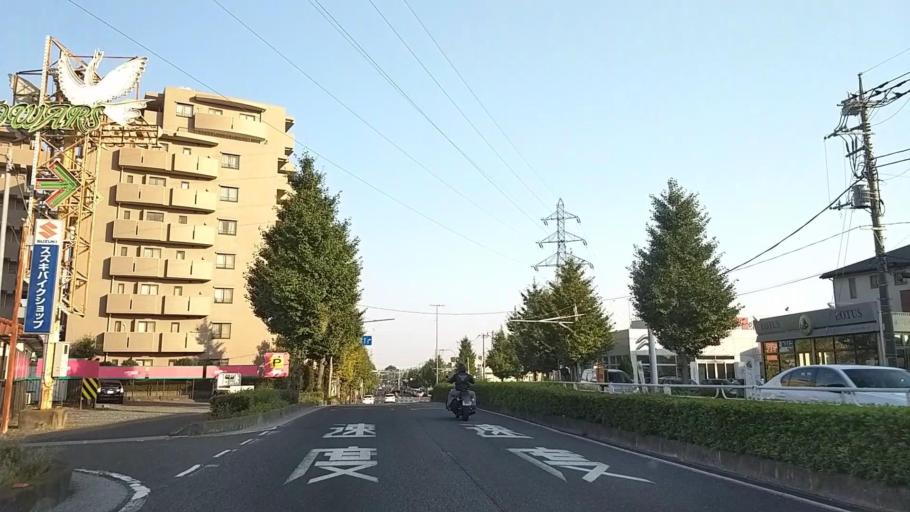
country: JP
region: Saitama
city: Tokorozawa
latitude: 35.7957
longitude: 139.4338
